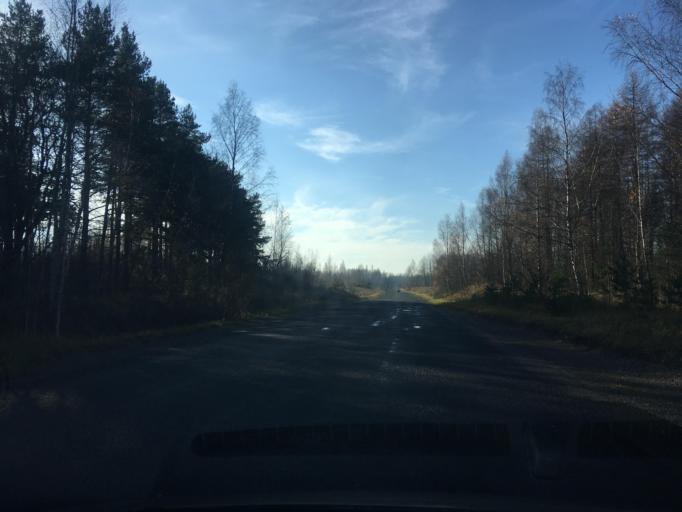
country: EE
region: Harju
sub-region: Maardu linn
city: Maardu
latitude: 59.4664
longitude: 25.0246
